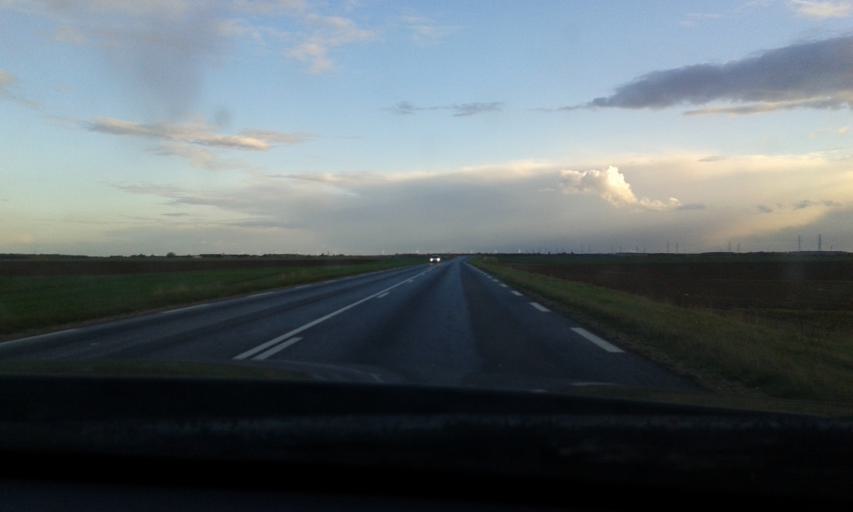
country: FR
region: Centre
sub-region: Departement d'Eure-et-Loir
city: Janville
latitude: 48.2479
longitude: 1.7716
